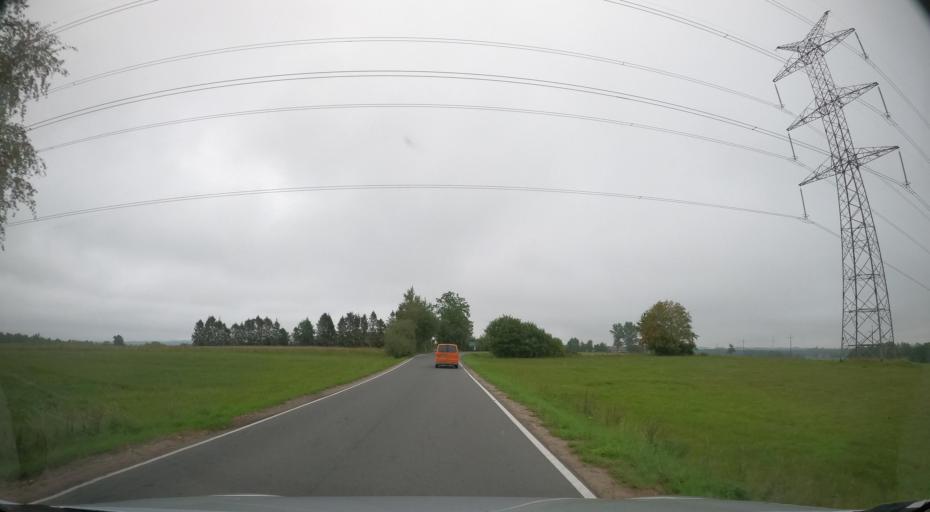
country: PL
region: Pomeranian Voivodeship
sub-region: Powiat wejherowski
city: Szemud
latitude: 54.5001
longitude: 18.1761
